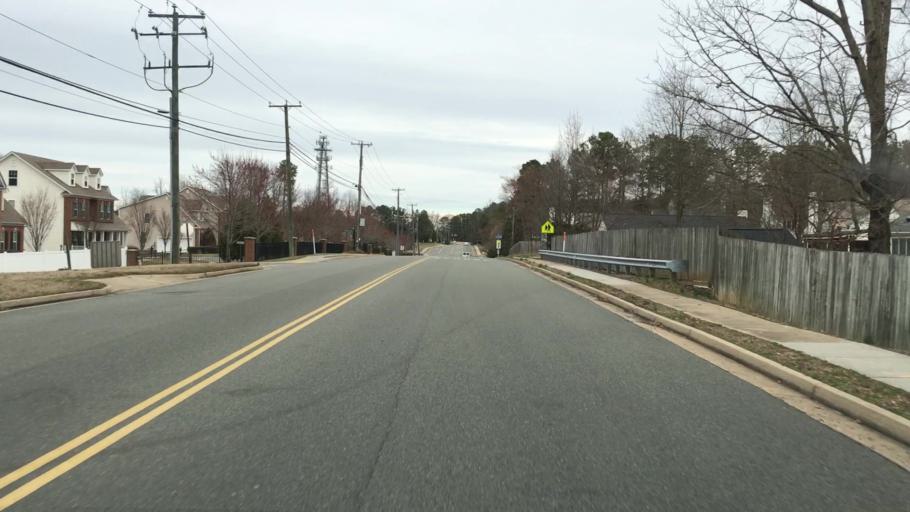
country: US
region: Virginia
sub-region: Henrico County
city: Glen Allen
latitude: 37.6644
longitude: -77.5436
